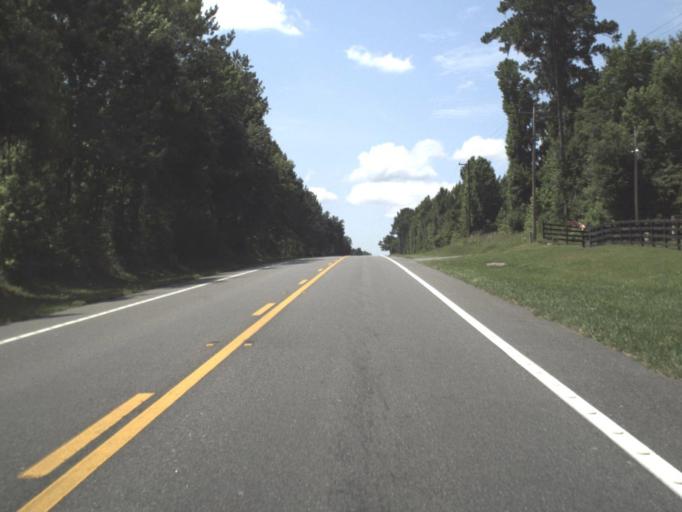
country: US
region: Florida
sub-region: Levy County
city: Williston
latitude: 29.4495
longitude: -82.4109
